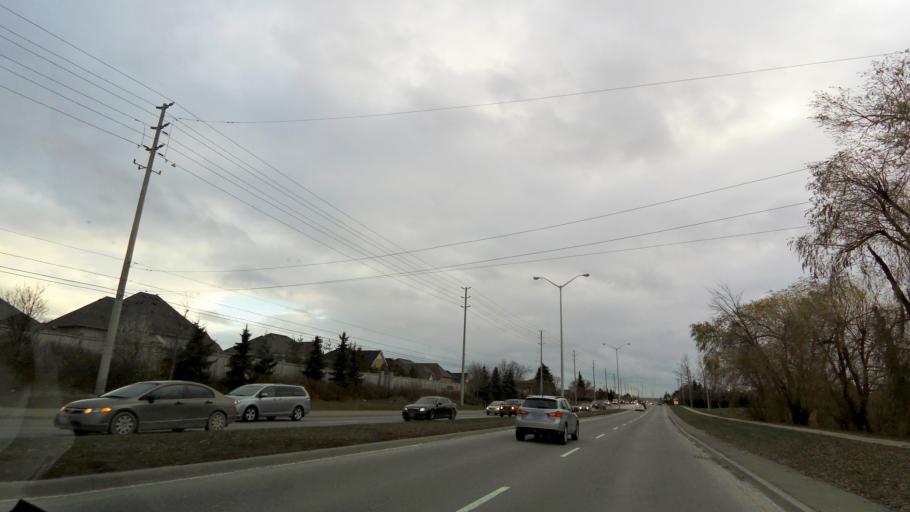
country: CA
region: Ontario
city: Brampton
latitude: 43.7813
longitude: -79.7018
